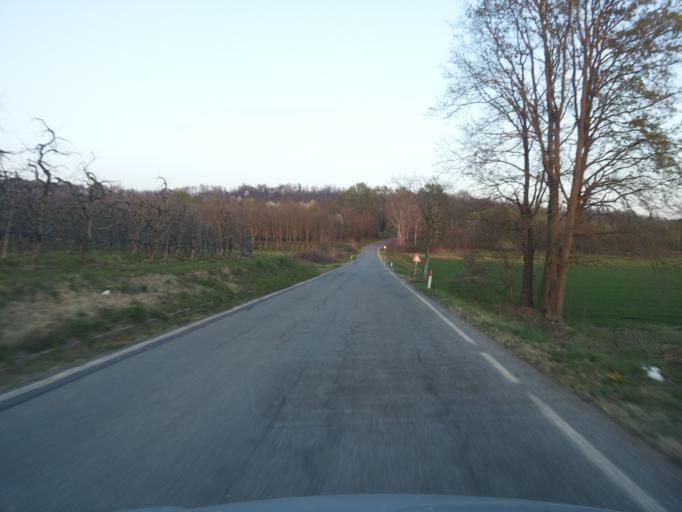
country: IT
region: Piedmont
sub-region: Provincia di Torino
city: Maglione
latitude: 45.3532
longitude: 8.0015
